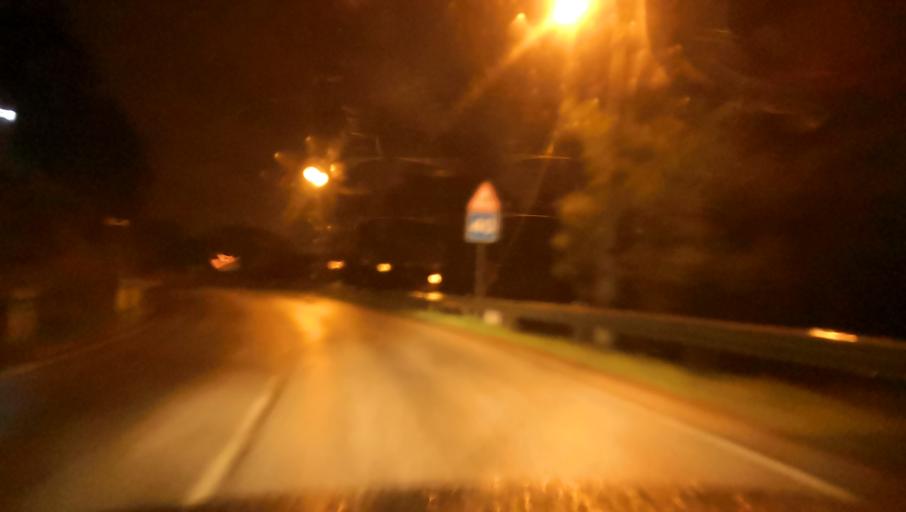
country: PT
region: Vila Real
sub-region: Vila Real
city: Vila Real
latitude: 41.3387
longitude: -7.7275
